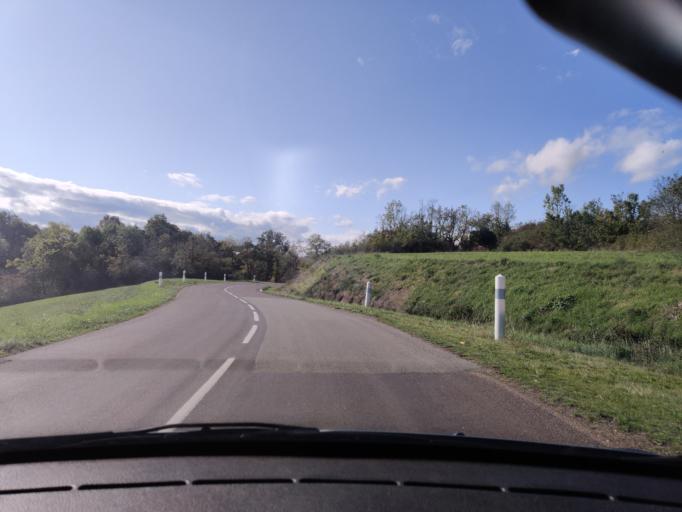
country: FR
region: Auvergne
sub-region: Departement du Puy-de-Dome
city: Combronde
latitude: 45.9969
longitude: 3.1371
